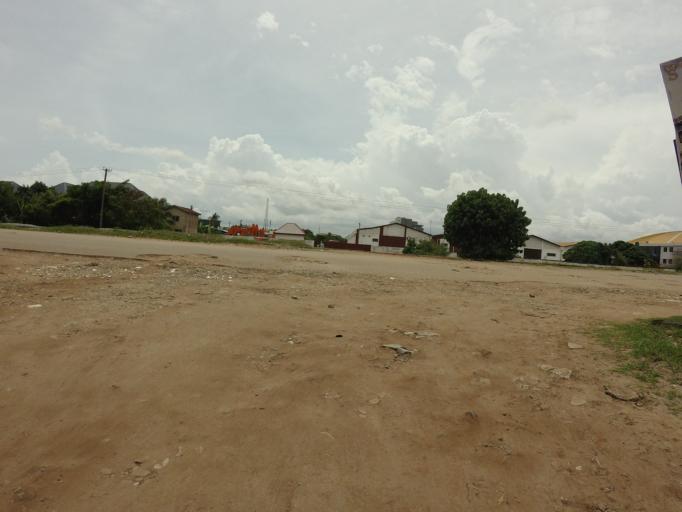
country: GH
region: Greater Accra
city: Accra
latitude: 5.6051
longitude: -0.2092
